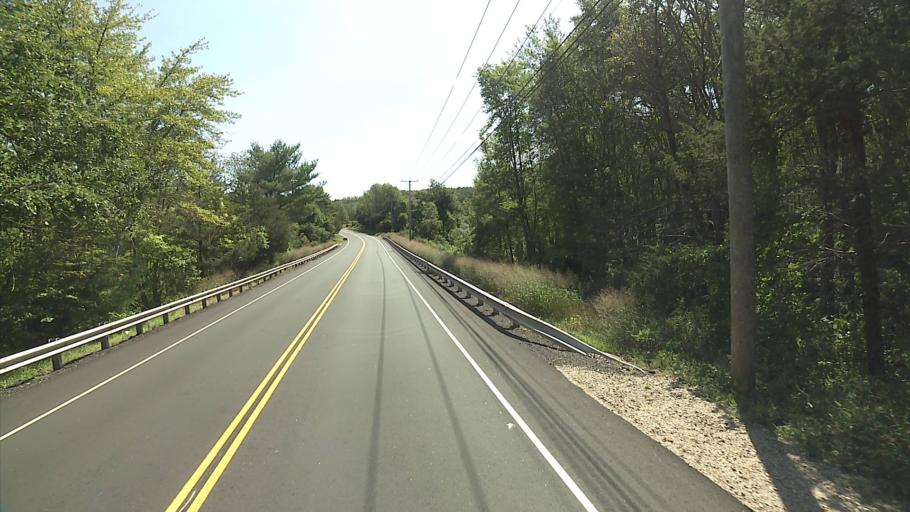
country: US
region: Connecticut
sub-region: New London County
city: Jewett City
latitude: 41.5824
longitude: -71.9054
